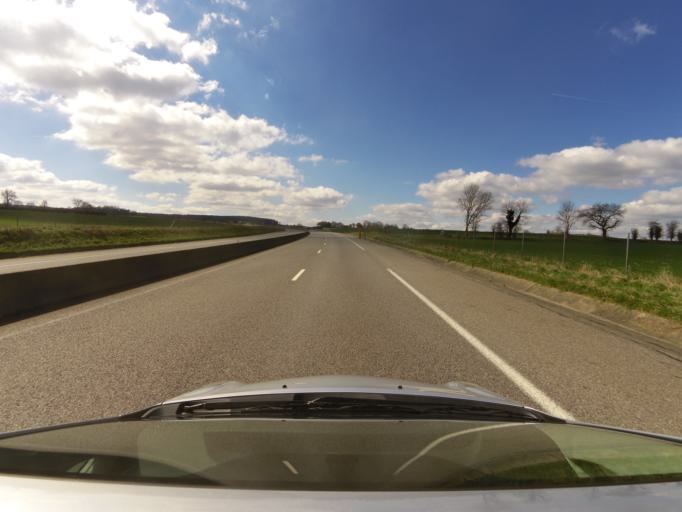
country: FR
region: Haute-Normandie
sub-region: Departement de la Seine-Maritime
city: Neufchatel-en-Bray
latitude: 49.7817
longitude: 1.4782
